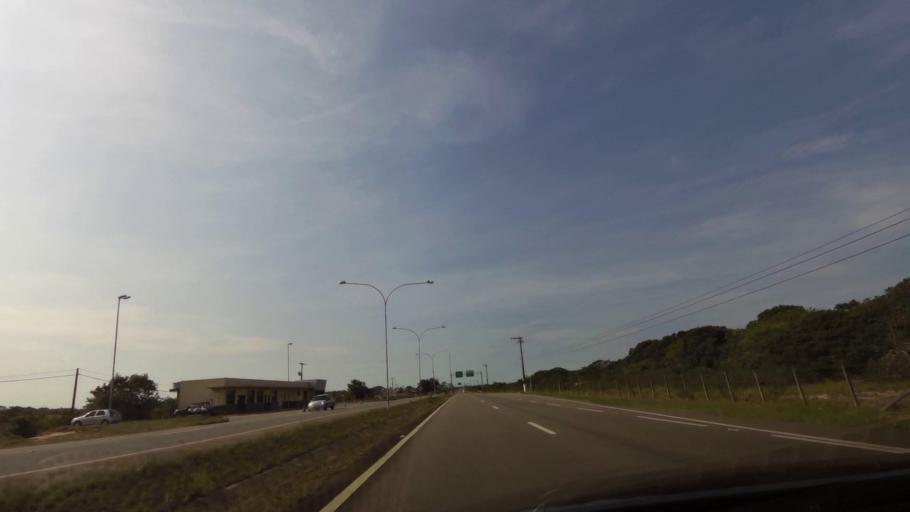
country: BR
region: Espirito Santo
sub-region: Guarapari
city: Guarapari
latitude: -20.5495
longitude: -40.3982
